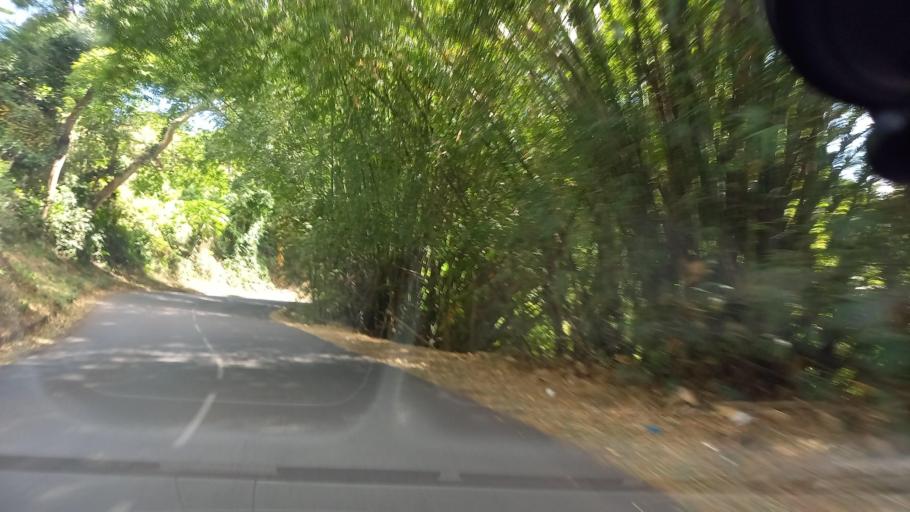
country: YT
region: Mamoudzou
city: Mamoudzou
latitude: -12.7958
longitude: 45.1969
